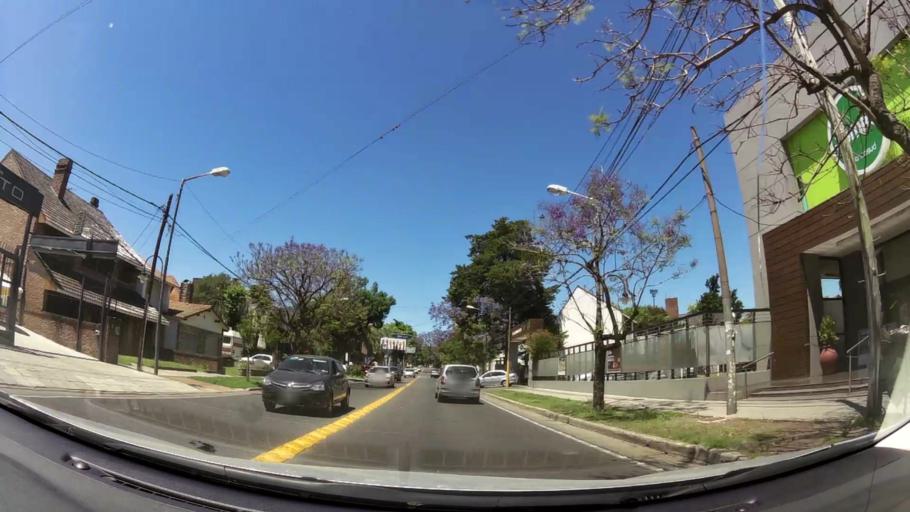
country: AR
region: Buenos Aires
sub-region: Partido de Tigre
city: Tigre
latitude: -34.4467
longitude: -58.5454
